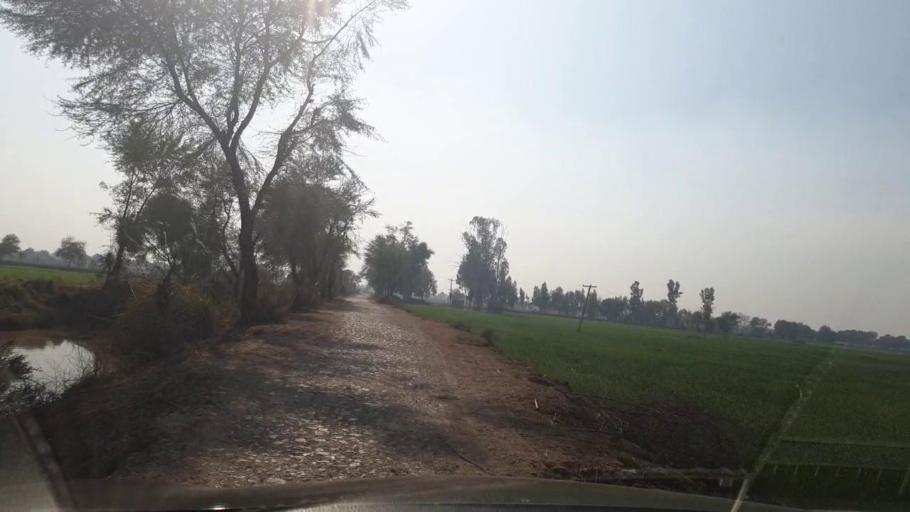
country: PK
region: Sindh
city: Khairpur
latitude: 28.1283
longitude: 69.6452
